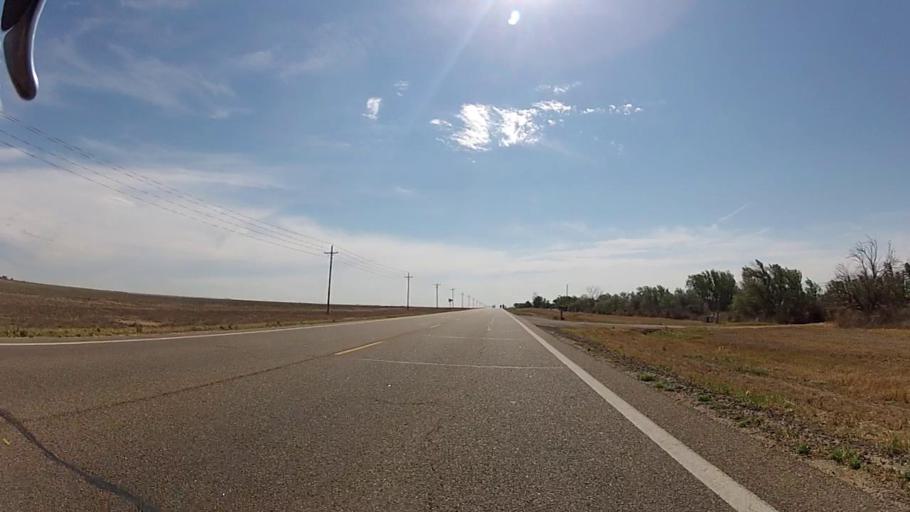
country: US
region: Kansas
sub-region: Grant County
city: Ulysses
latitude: 37.5617
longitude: -101.2969
